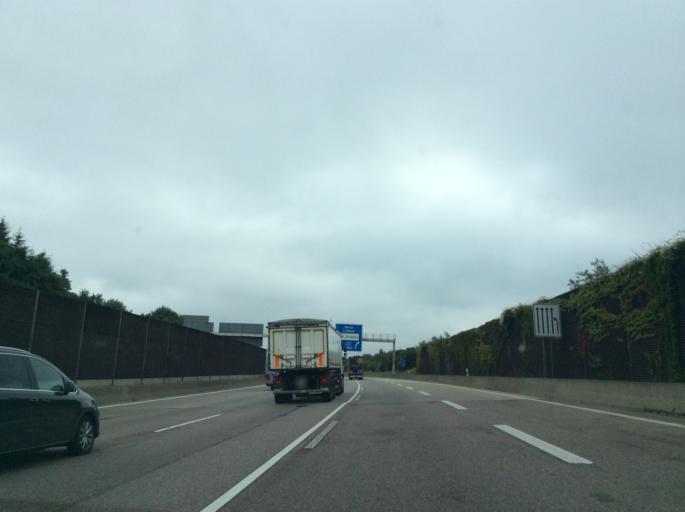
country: DE
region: Saxony
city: Albertstadt
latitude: 51.1098
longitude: 13.7390
